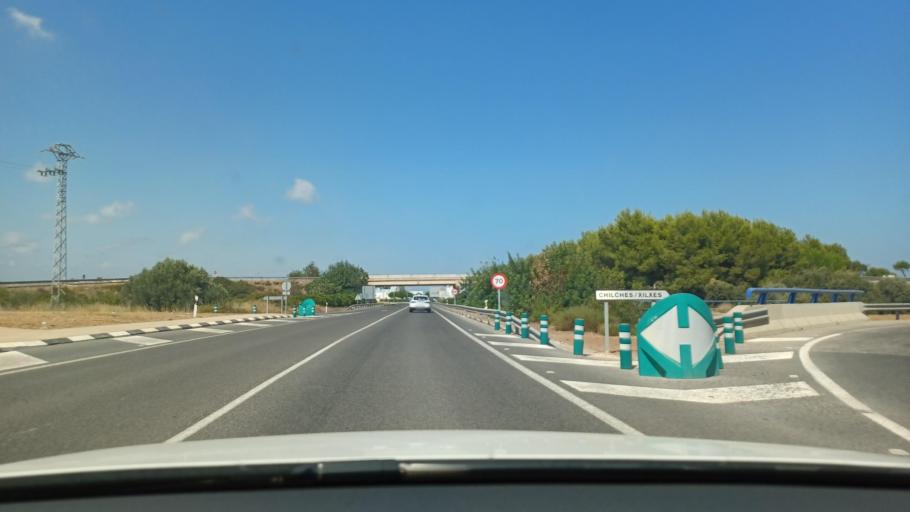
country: ES
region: Valencia
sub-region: Provincia de Castello
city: Chilches
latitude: 39.7791
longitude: -0.1959
